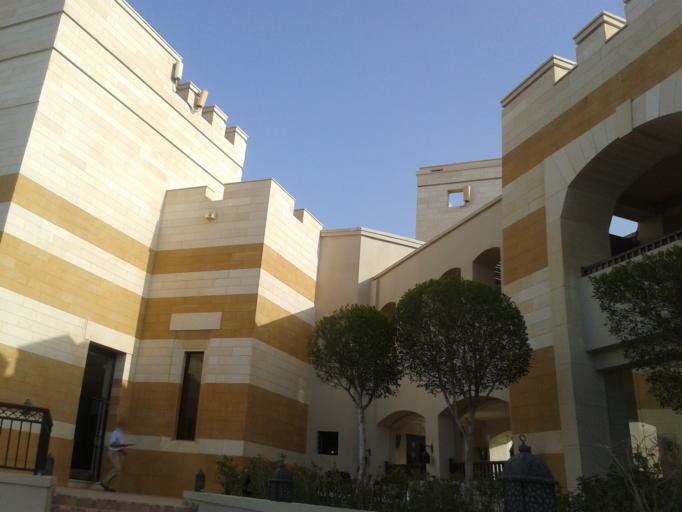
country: EG
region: Red Sea
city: Marsa Alam
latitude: 25.5359
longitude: 34.6391
